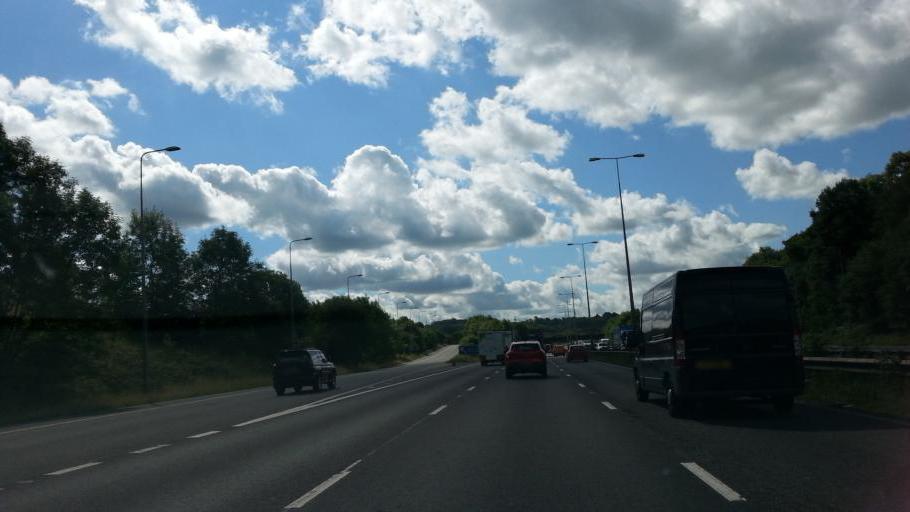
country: GB
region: England
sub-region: Leicestershire
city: Shepshed
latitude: 52.7645
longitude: -1.2742
